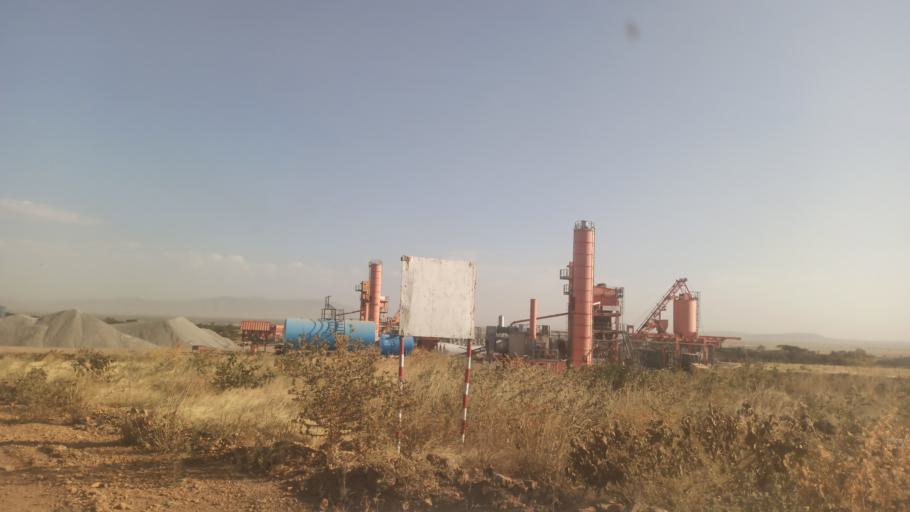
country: ET
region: Oromiya
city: Ziway
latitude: 7.9322
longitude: 38.6162
